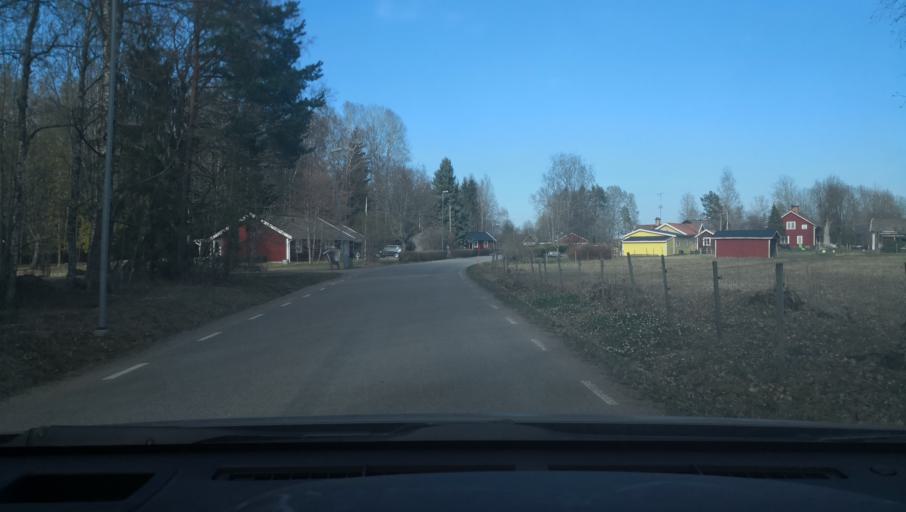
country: SE
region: Uppsala
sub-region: Heby Kommun
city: Heby
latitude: 59.9225
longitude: 16.8493
